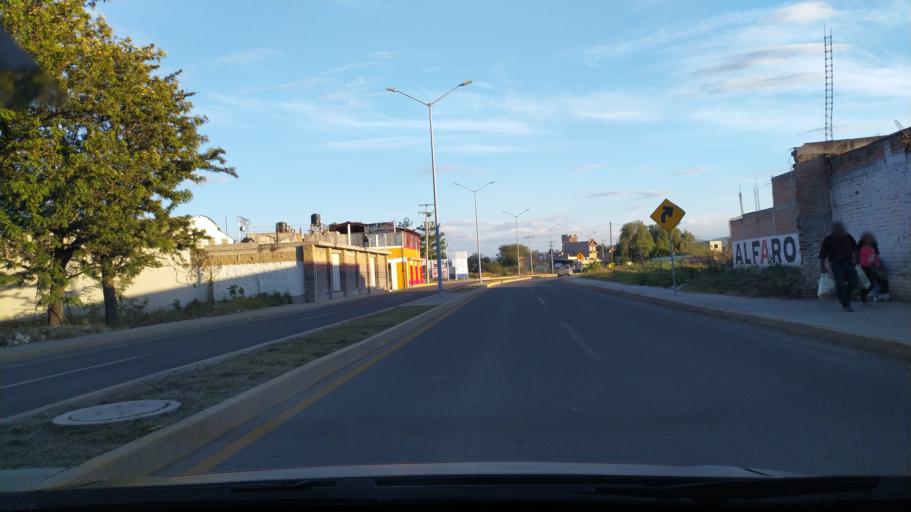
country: MX
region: Guanajuato
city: Ciudad Manuel Doblado
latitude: 20.7333
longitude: -101.9470
